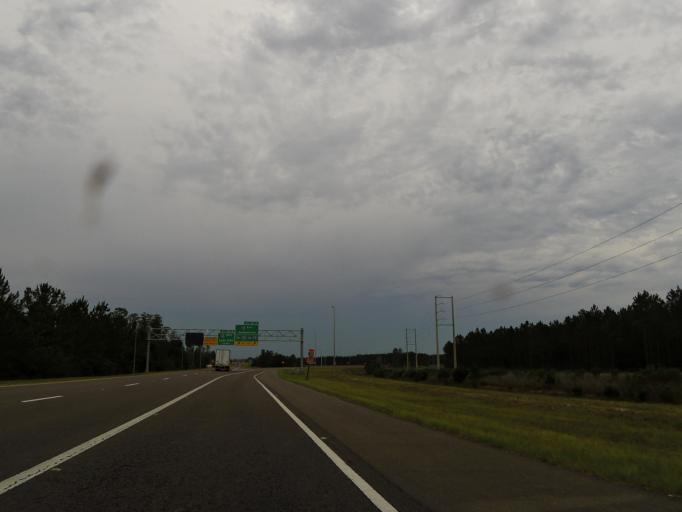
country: US
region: Florida
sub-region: Duval County
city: Baldwin
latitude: 30.2976
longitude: -81.8783
